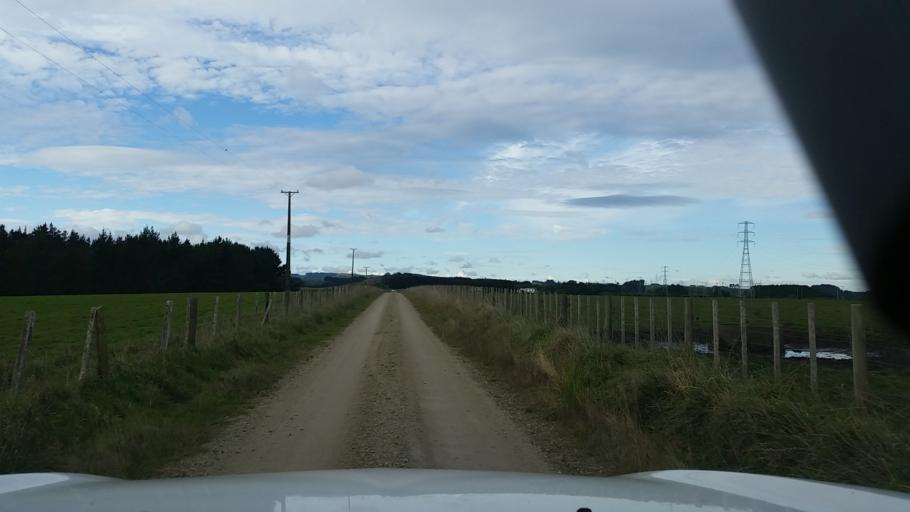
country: NZ
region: Taranaki
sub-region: South Taranaki District
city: Patea
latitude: -39.7894
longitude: 174.7485
